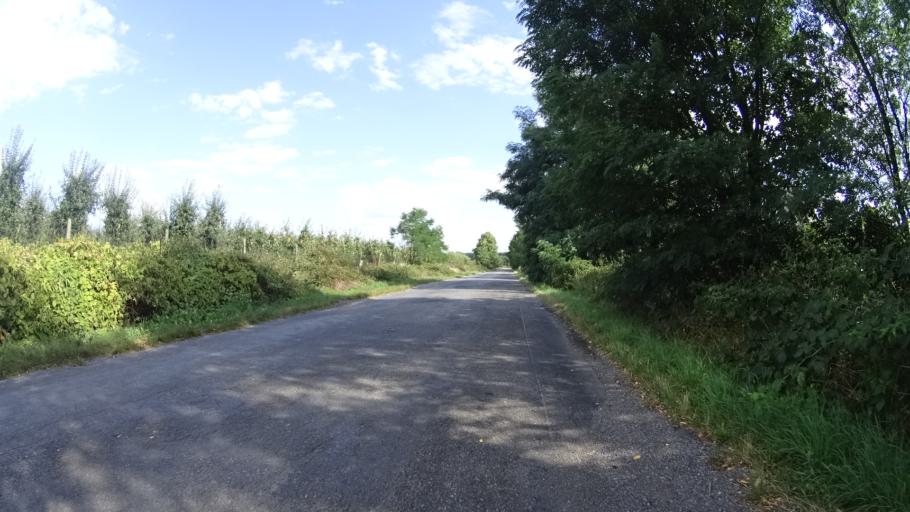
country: PL
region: Masovian Voivodeship
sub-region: Powiat grojecki
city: Mogielnica
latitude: 51.6833
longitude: 20.7597
